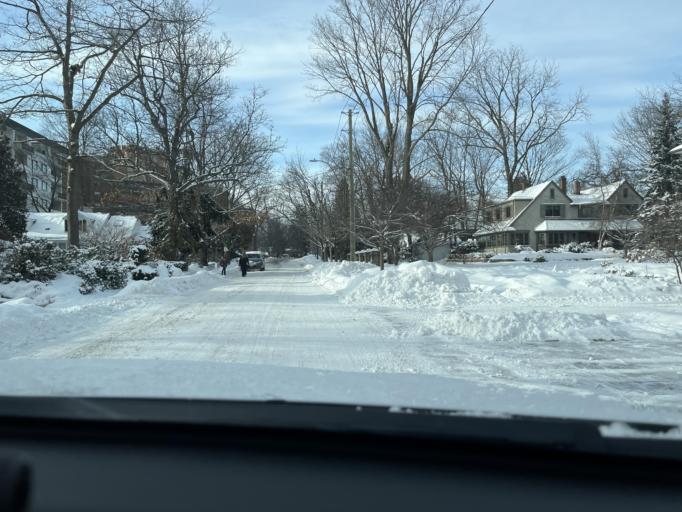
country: CA
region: Ontario
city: Oakville
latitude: 43.4491
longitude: -79.6628
